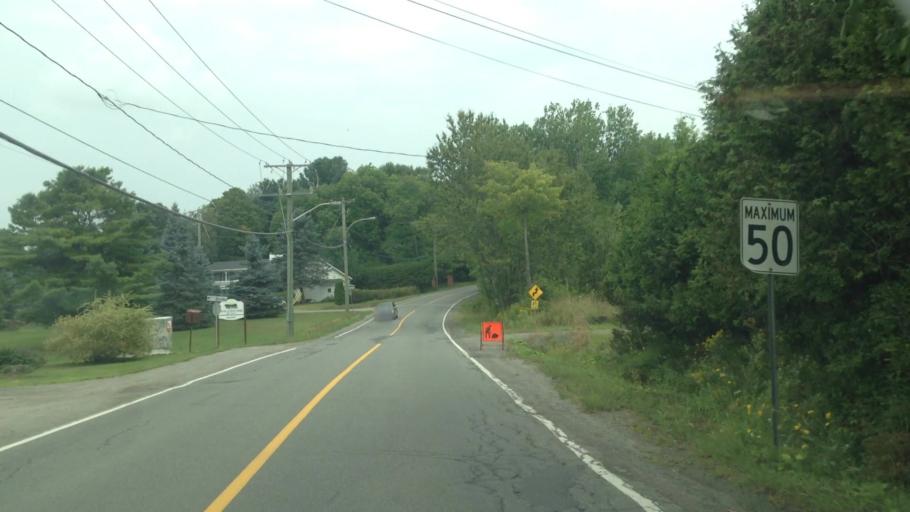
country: CA
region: Quebec
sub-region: Laurentides
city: Saint-Jerome
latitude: 45.8185
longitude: -73.9702
